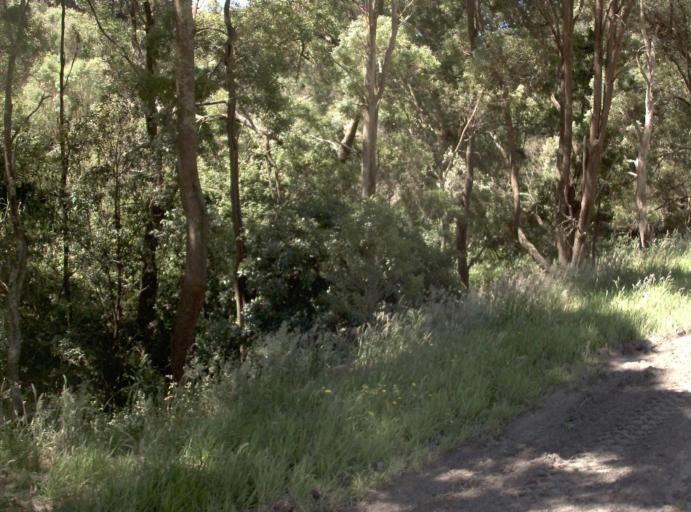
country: AU
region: Victoria
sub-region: Bass Coast
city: North Wonthaggi
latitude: -38.6955
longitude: 146.0959
